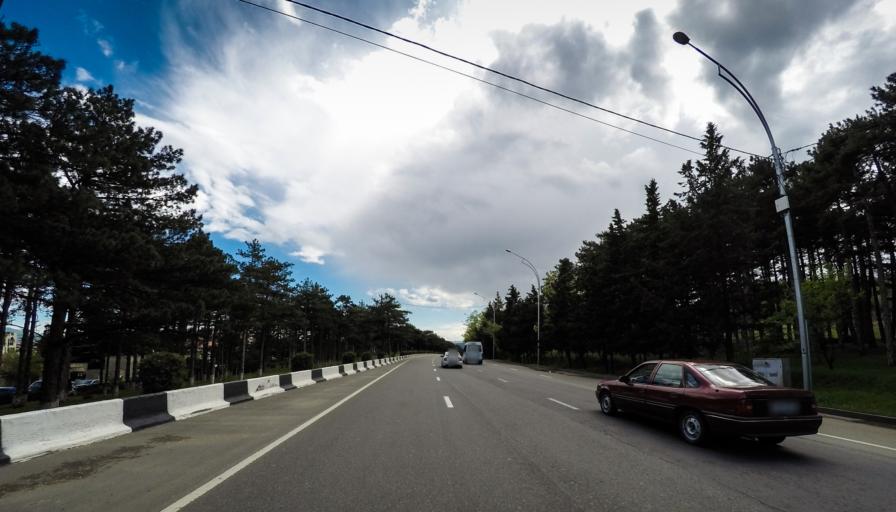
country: GE
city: Zahesi
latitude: 41.8151
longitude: 44.7714
